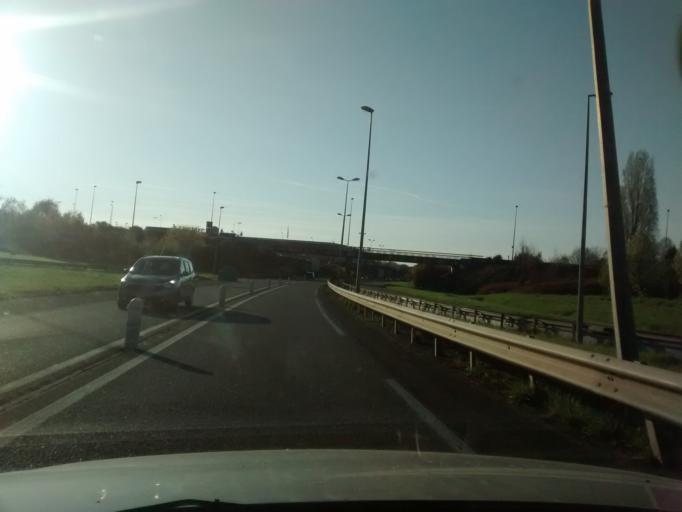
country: FR
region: Pays de la Loire
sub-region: Departement de la Sarthe
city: Sarge-les-le-Mans
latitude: 48.0214
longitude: 0.2311
